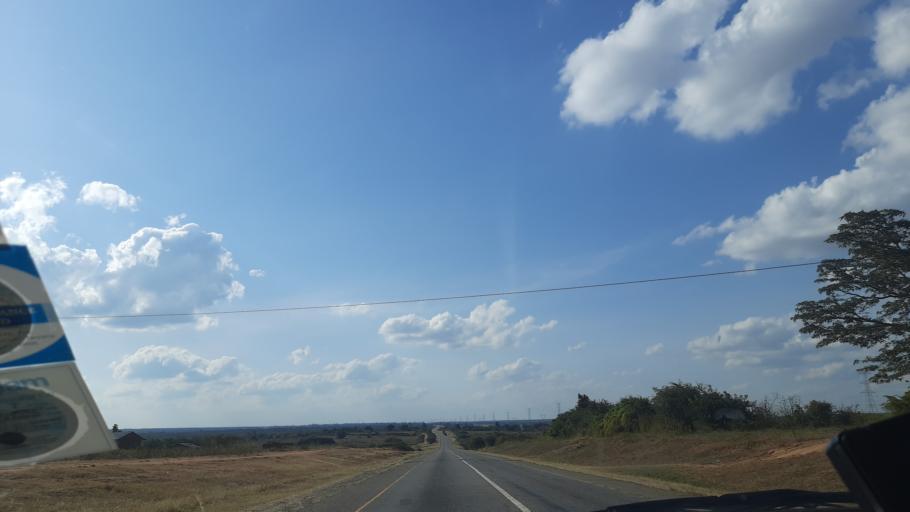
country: TZ
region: Singida
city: Ikungi
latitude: -5.2001
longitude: 34.7843
